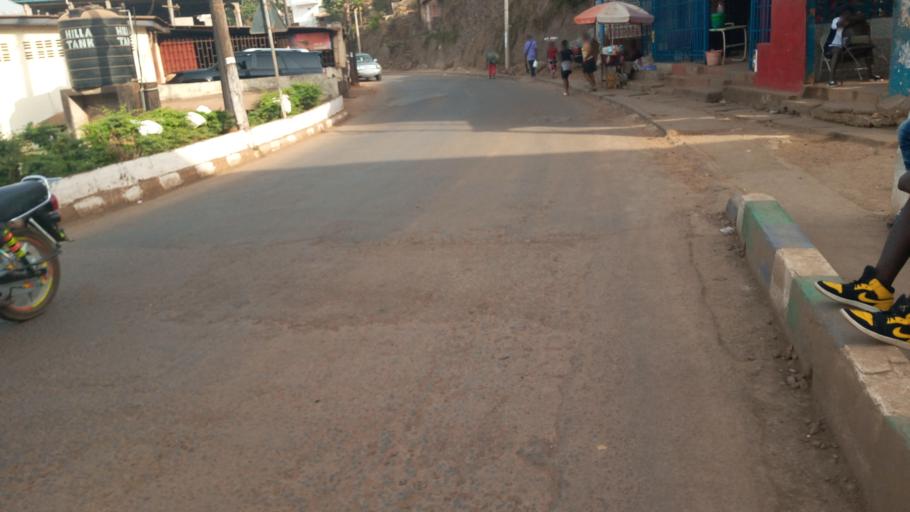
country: SL
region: Western Area
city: Freetown
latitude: 8.4753
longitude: -13.2584
